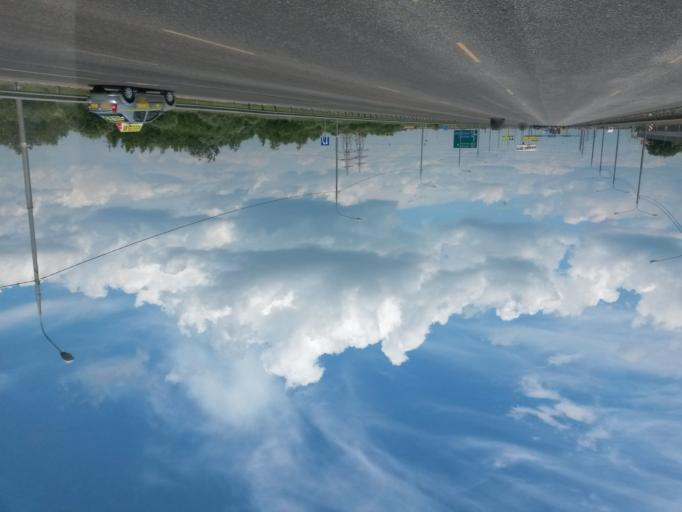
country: RU
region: Moskovskaya
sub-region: Podol'skiy Rayon
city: Podol'sk
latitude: 55.4276
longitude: 37.6135
